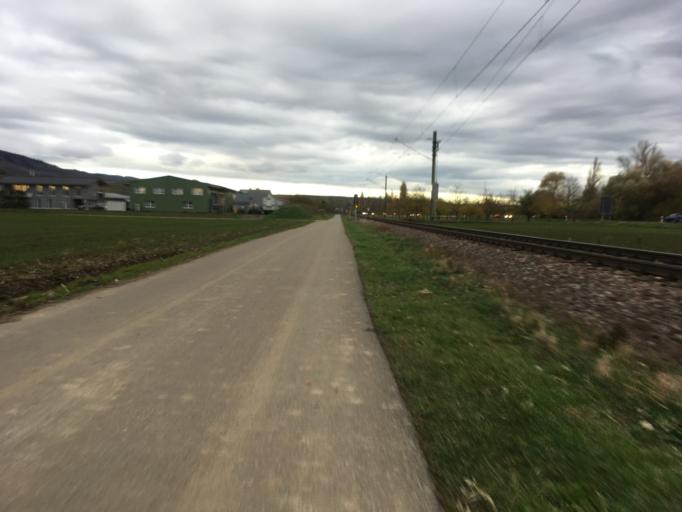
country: DE
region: Baden-Wuerttemberg
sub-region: Freiburg Region
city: Gottenheim
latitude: 48.0587
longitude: 7.7237
